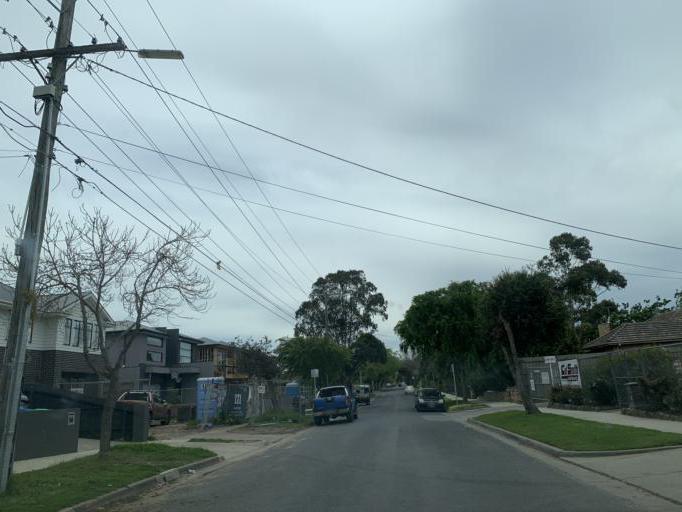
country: AU
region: Victoria
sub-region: Bayside
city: Highett
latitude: -37.9546
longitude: 145.0335
